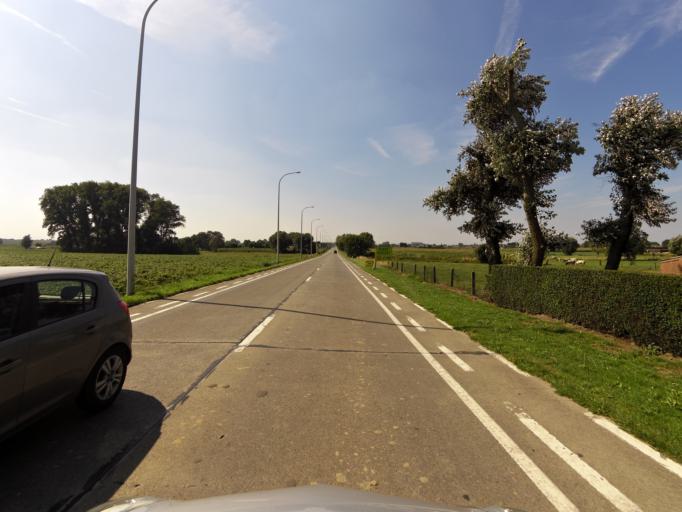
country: BE
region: Flanders
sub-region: Provincie West-Vlaanderen
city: Dentergem
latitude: 50.9936
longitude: 3.3970
